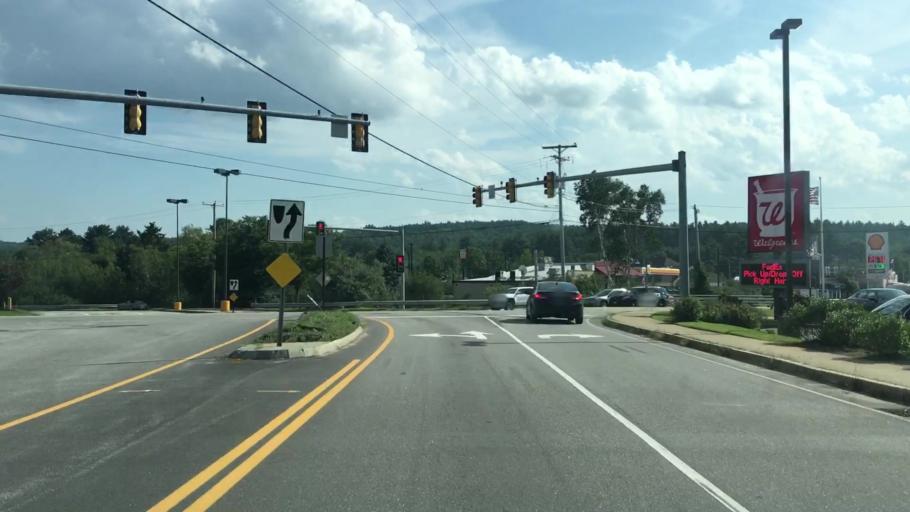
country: US
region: New Hampshire
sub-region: Belknap County
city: Tilton
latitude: 43.4568
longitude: -71.5654
